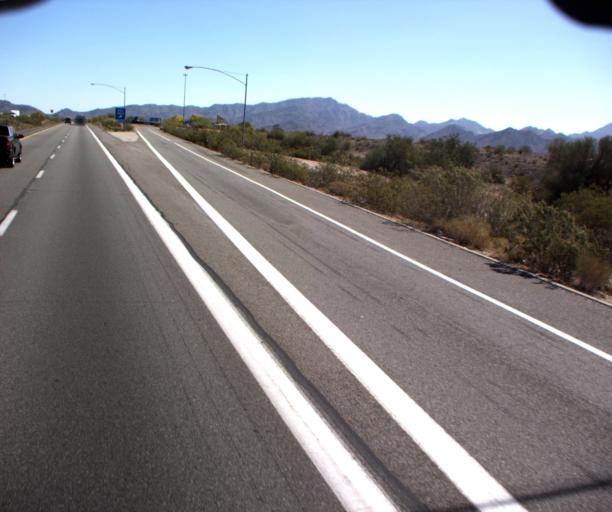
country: US
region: Arizona
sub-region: La Paz County
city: Ehrenberg
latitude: 33.6177
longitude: -114.4564
